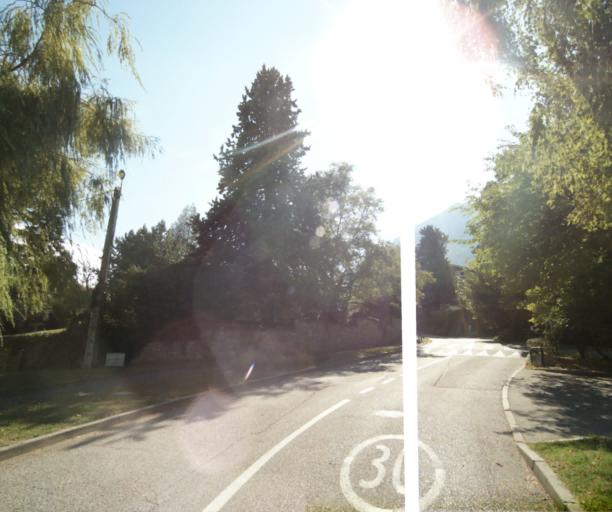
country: FR
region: Rhone-Alpes
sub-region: Departement de l'Isere
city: Seyssins
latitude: 45.1615
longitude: 5.6827
